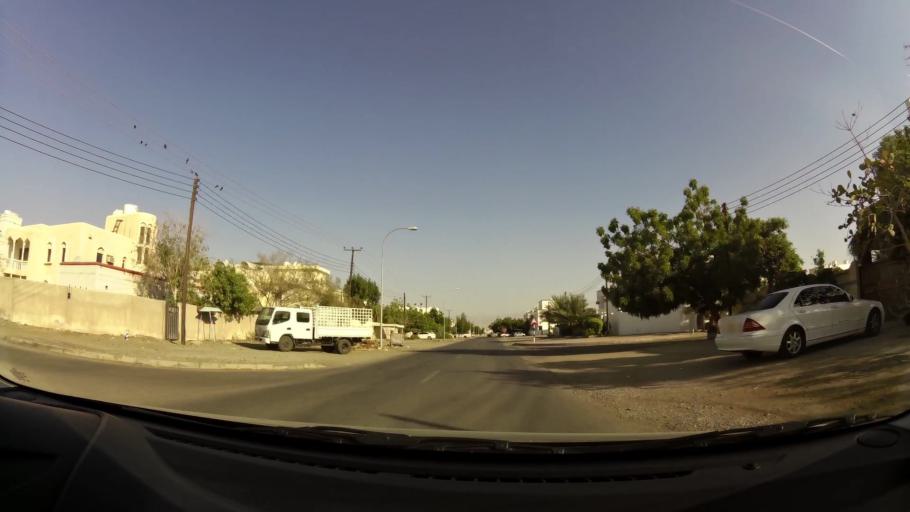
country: OM
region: Muhafazat Masqat
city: As Sib al Jadidah
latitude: 23.6343
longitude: 58.2056
